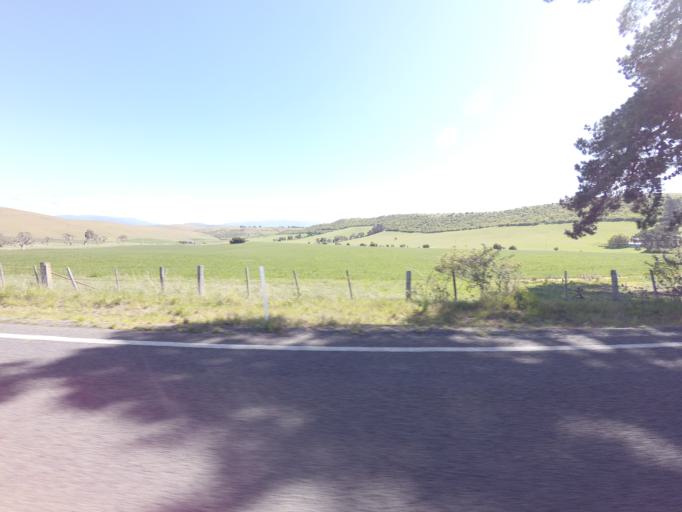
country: AU
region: Tasmania
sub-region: Derwent Valley
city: New Norfolk
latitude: -42.5666
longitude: 146.8808
